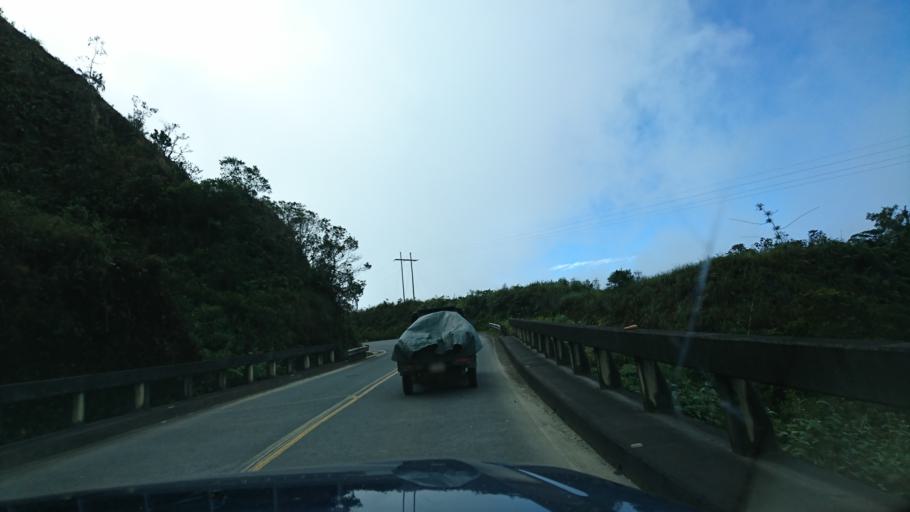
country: BO
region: La Paz
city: Coroico
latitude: -16.2545
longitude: -67.8357
